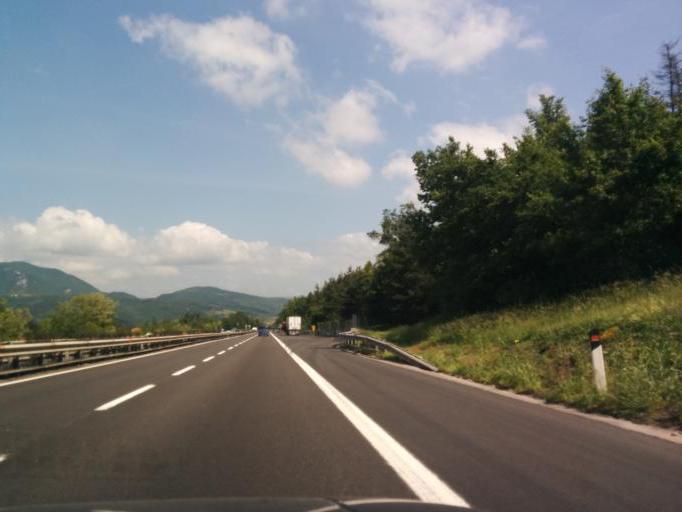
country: IT
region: Emilia-Romagna
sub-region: Provincia di Bologna
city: Grizzana
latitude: 44.2416
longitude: 11.1936
